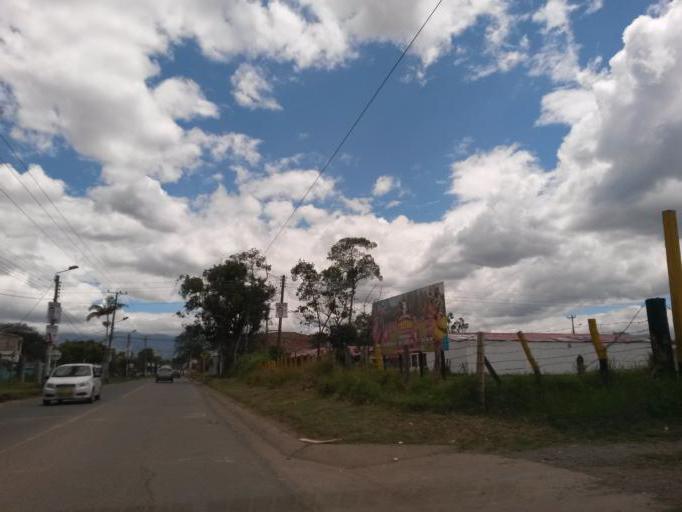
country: CO
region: Cauca
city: Popayan
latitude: 2.4869
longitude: -76.5858
